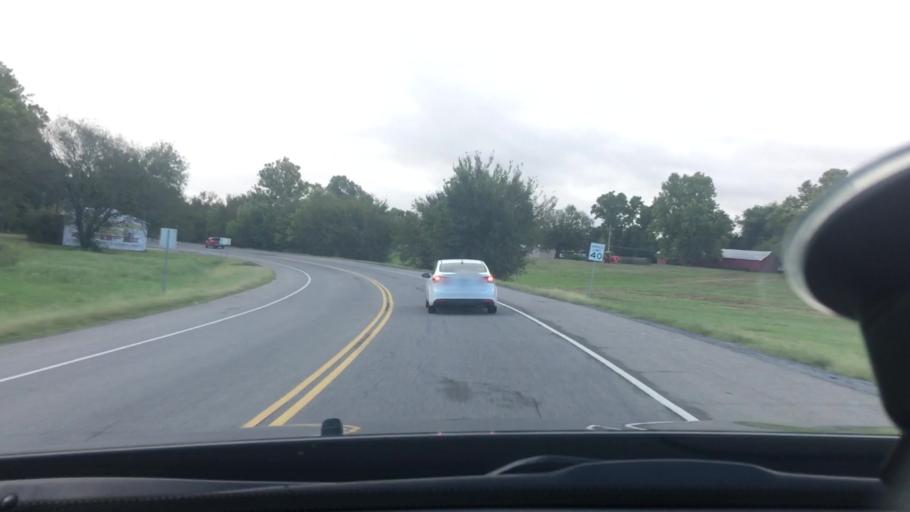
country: US
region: Oklahoma
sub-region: Coal County
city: Coalgate
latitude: 34.5430
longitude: -96.2281
